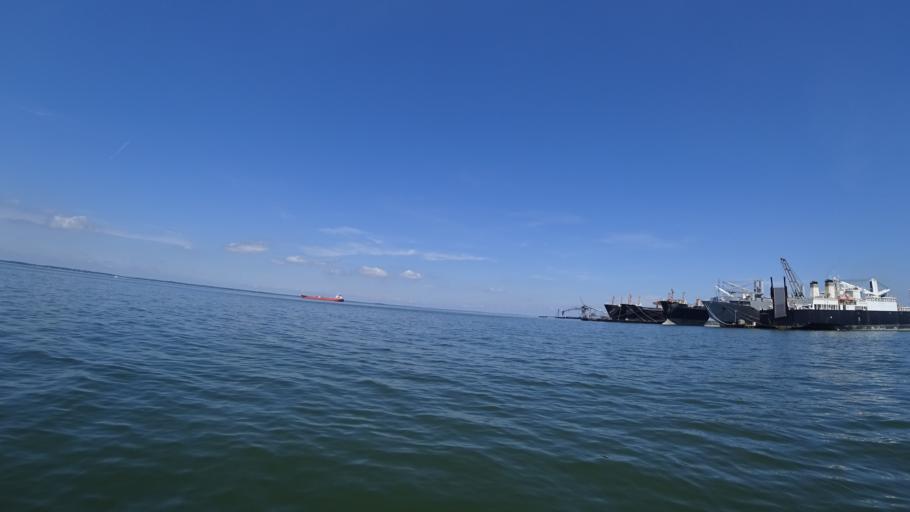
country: US
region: Virginia
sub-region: City of Newport News
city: Newport News
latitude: 36.9586
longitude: -76.4161
